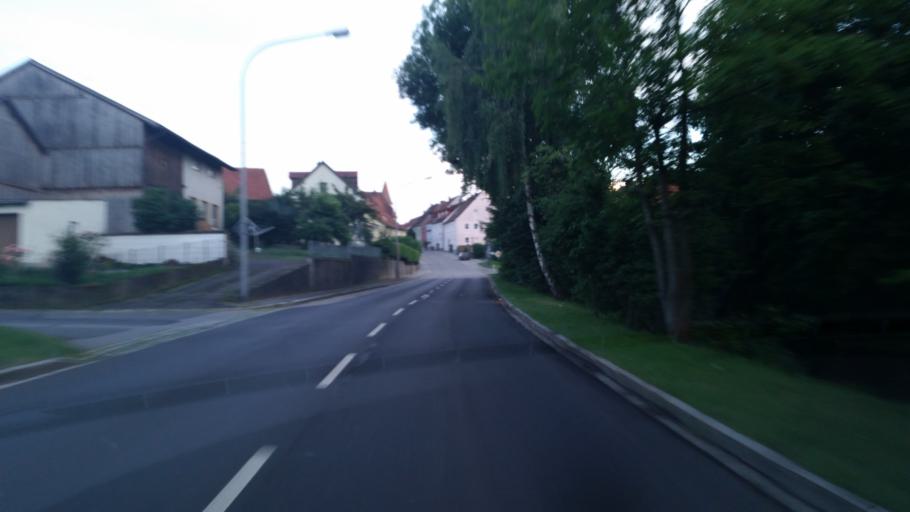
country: DE
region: Bavaria
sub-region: Upper Palatinate
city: Luhe-Wildenau
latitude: 49.5854
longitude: 12.1489
